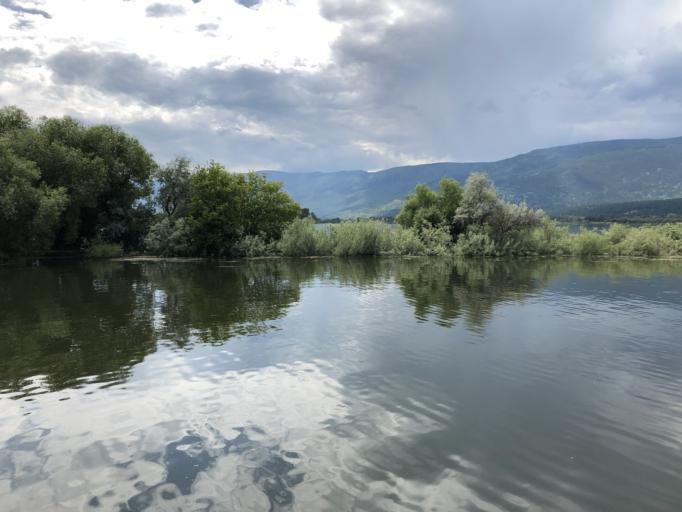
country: CA
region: British Columbia
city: Salmon Arm
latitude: 50.7074
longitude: -119.2837
